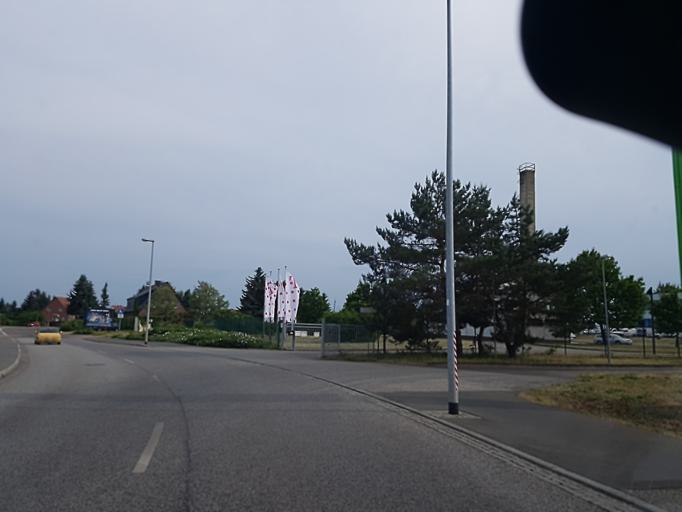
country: DE
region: Saxony-Anhalt
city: Wittenburg
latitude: 51.8689
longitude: 12.6754
